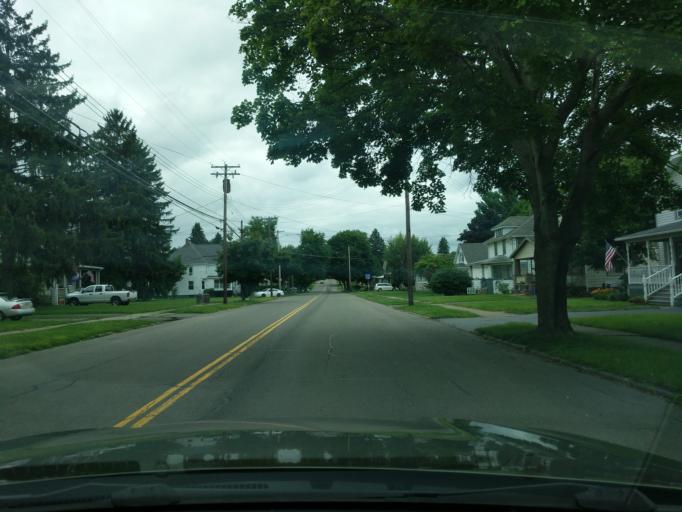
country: US
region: New York
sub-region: Chemung County
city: Elmira
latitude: 42.1065
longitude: -76.8188
